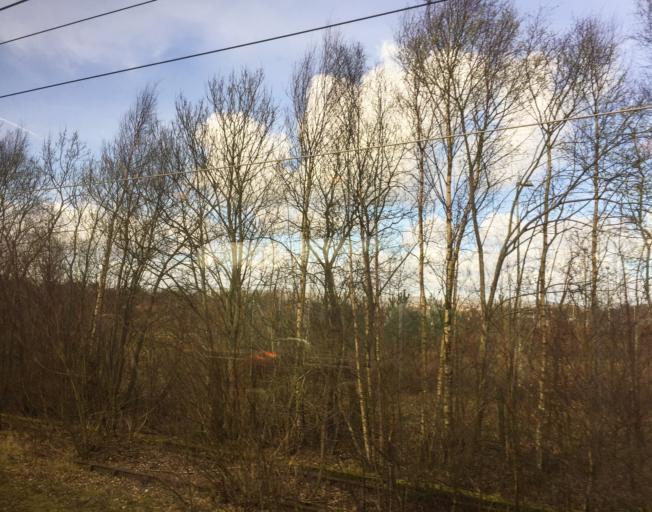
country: GB
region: Scotland
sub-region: North Lanarkshire
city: Glenboig
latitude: 55.8849
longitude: -4.0744
